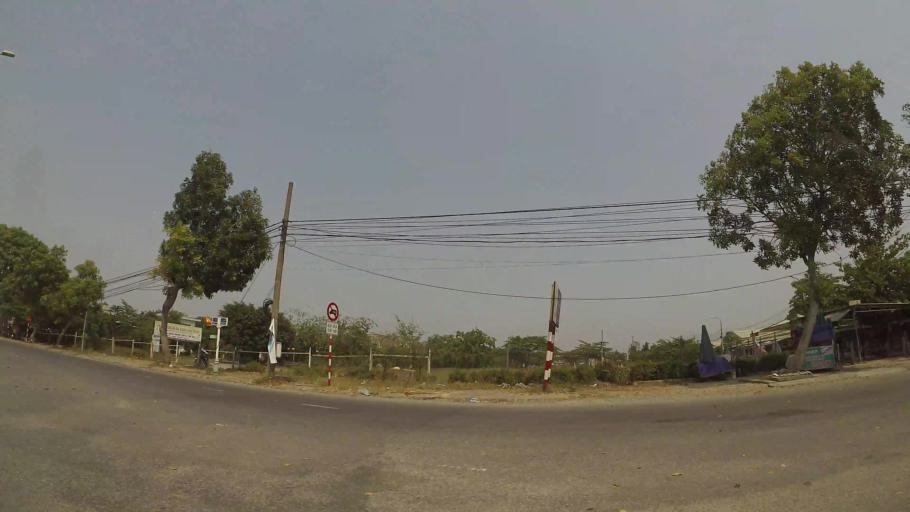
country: VN
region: Da Nang
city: Cam Le
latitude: 15.9804
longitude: 108.2081
